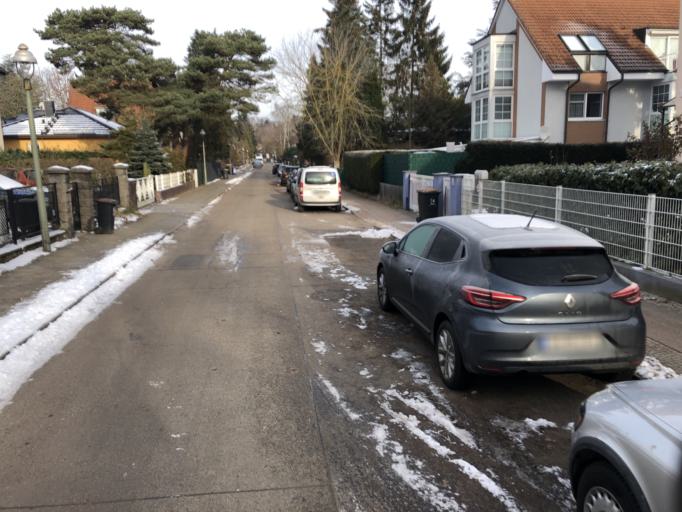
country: DE
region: Berlin
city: Hermsdorf
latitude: 52.6248
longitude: 13.3082
